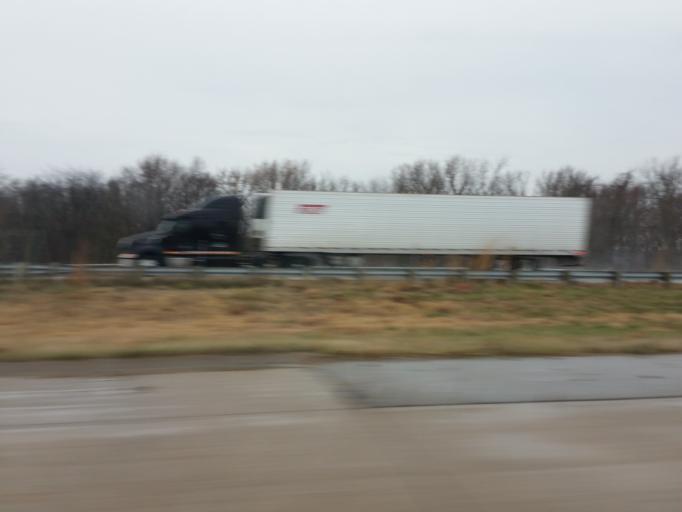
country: US
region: Iowa
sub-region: Cedar County
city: Tipton
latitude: 41.6457
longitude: -91.1359
